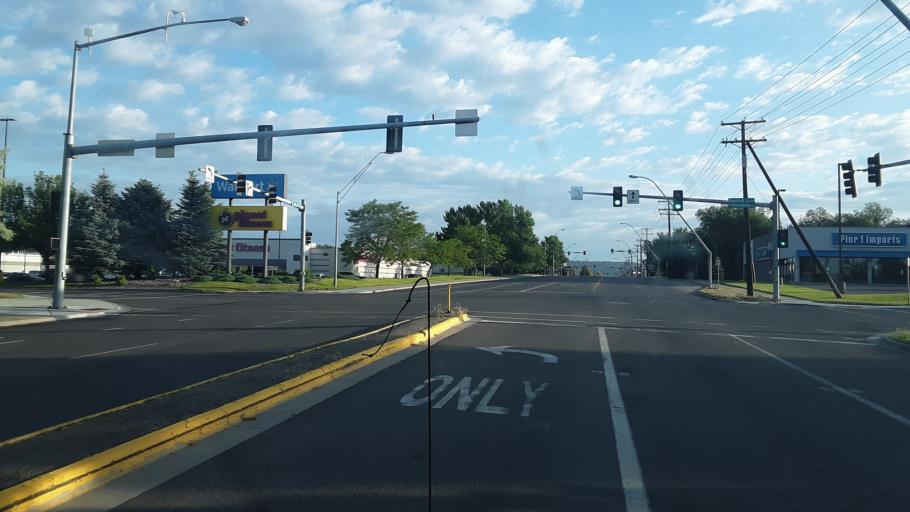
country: US
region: Montana
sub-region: Yellowstone County
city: Billings
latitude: 45.7567
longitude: -108.5761
